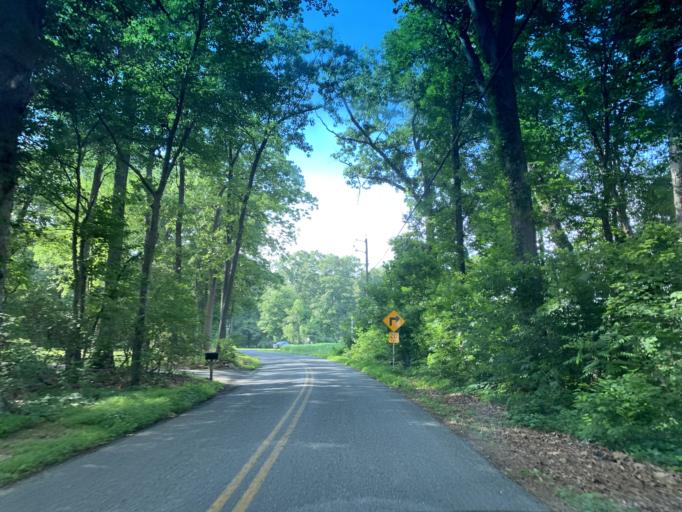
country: US
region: Maryland
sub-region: Harford County
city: Jarrettsville
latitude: 39.6518
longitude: -76.4162
